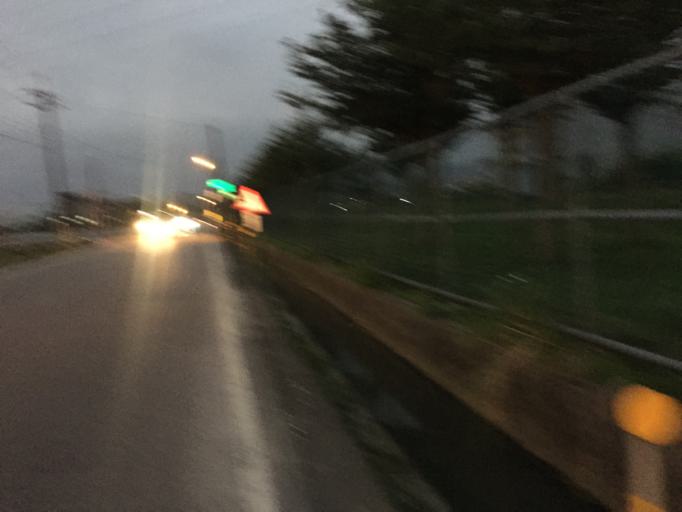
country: TW
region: Taiwan
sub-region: Yilan
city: Yilan
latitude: 24.6589
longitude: 121.7793
